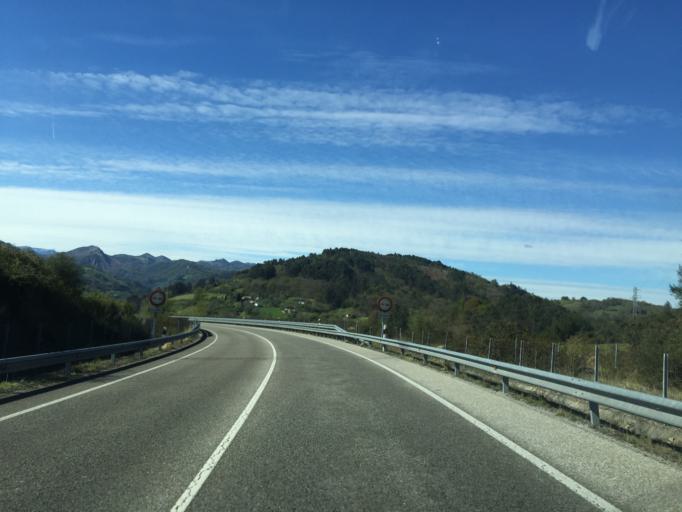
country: ES
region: Asturias
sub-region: Province of Asturias
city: Llanera
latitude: 43.3654
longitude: -5.9587
